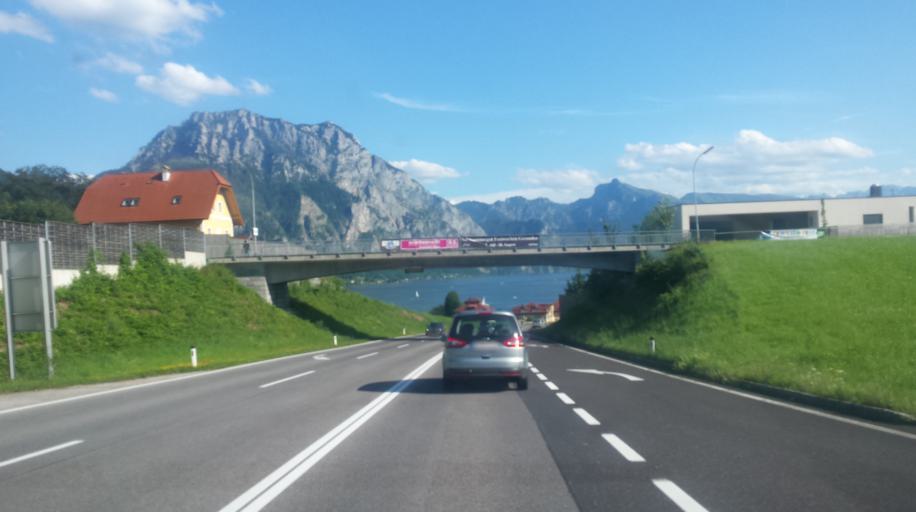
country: AT
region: Upper Austria
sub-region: Politischer Bezirk Gmunden
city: Altmunster
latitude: 47.9114
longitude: 13.7791
